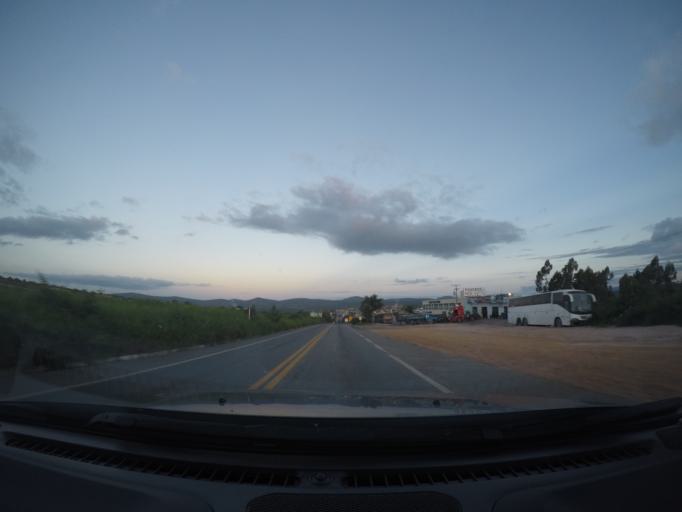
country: BR
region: Bahia
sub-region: Seabra
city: Seabra
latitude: -12.4294
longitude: -41.7891
